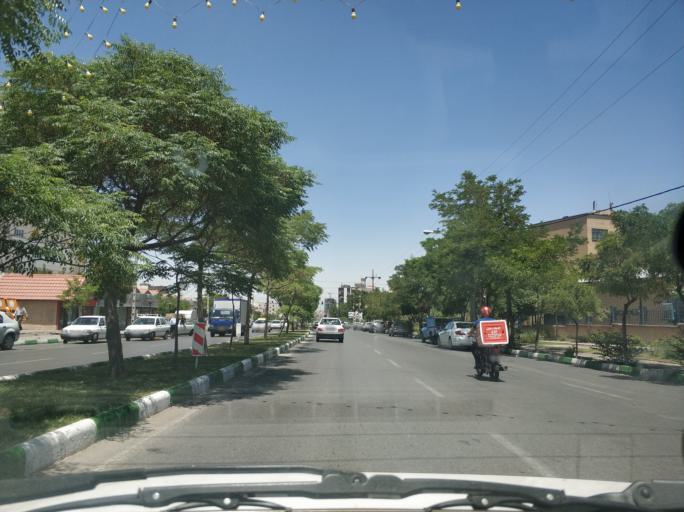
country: IR
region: Razavi Khorasan
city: Mashhad
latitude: 36.2992
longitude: 59.5096
